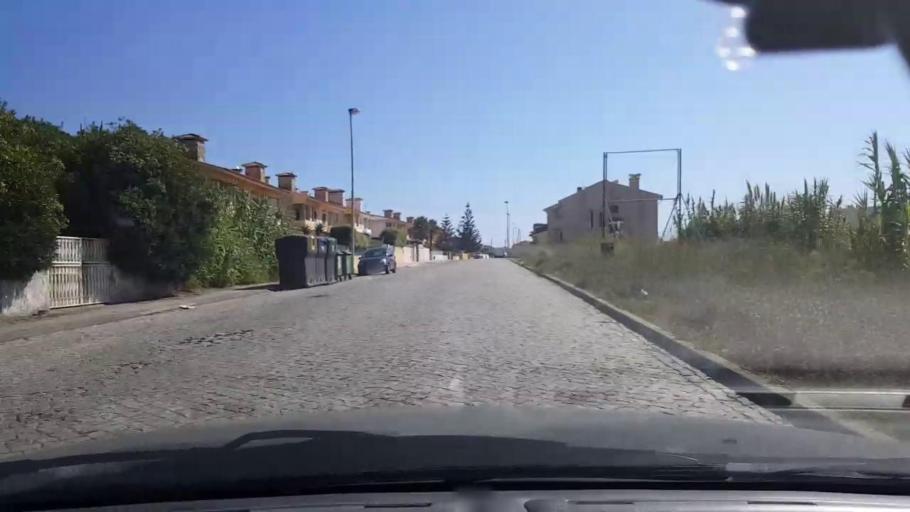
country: PT
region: Porto
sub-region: Vila do Conde
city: Arvore
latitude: 41.3029
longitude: -8.7359
